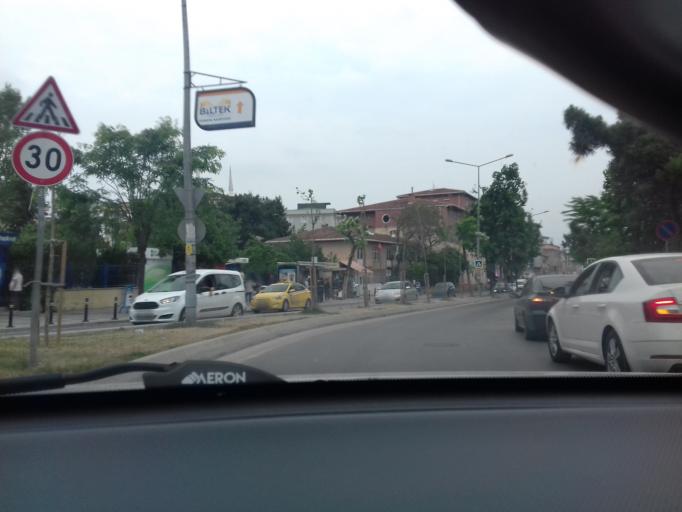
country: TR
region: Istanbul
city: Pendik
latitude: 40.9135
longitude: 29.2984
